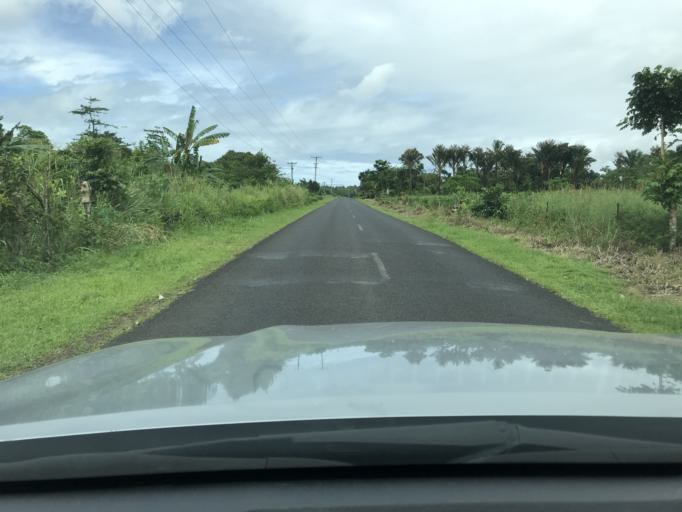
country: WS
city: Nofoali`i
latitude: -13.8753
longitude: -171.9313
